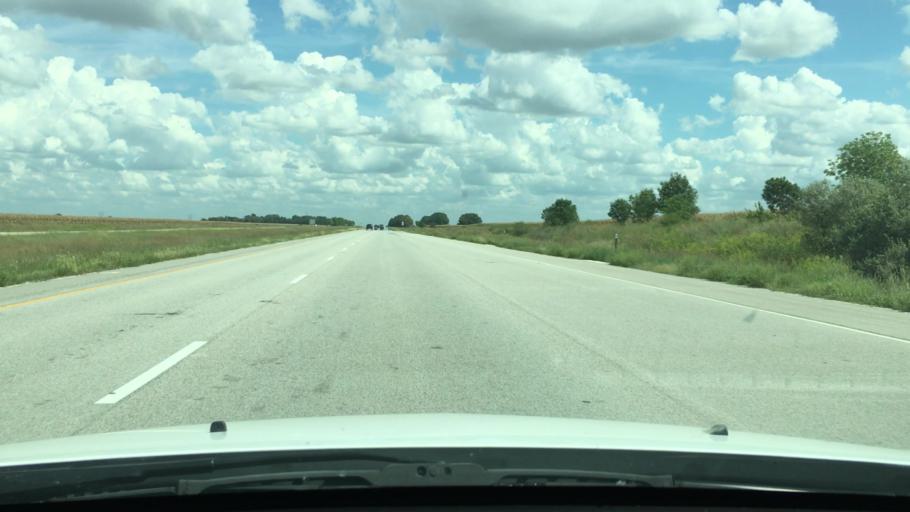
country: US
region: Illinois
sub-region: Sangamon County
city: New Berlin
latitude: 39.7368
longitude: -90.0359
